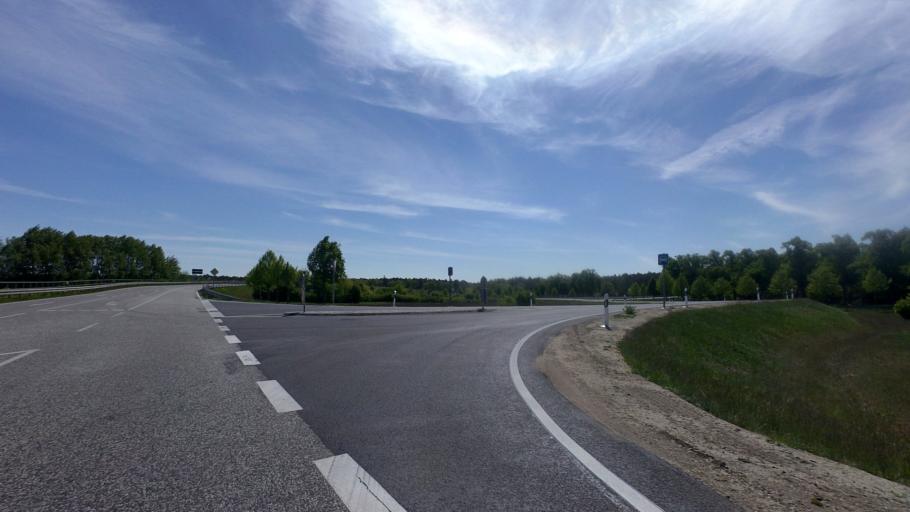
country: DE
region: Brandenburg
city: Luckenwalde
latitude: 52.1178
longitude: 13.1373
